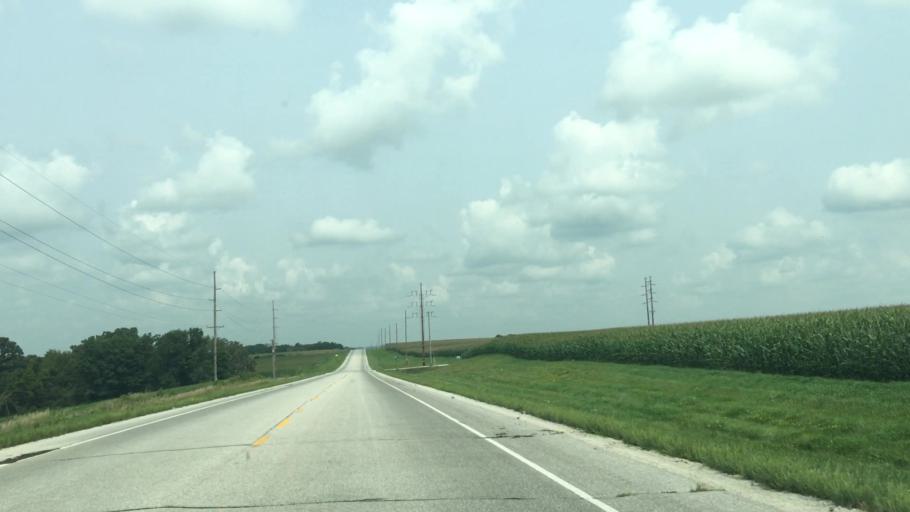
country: US
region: Minnesota
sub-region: Fillmore County
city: Harmony
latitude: 43.5640
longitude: -91.9297
